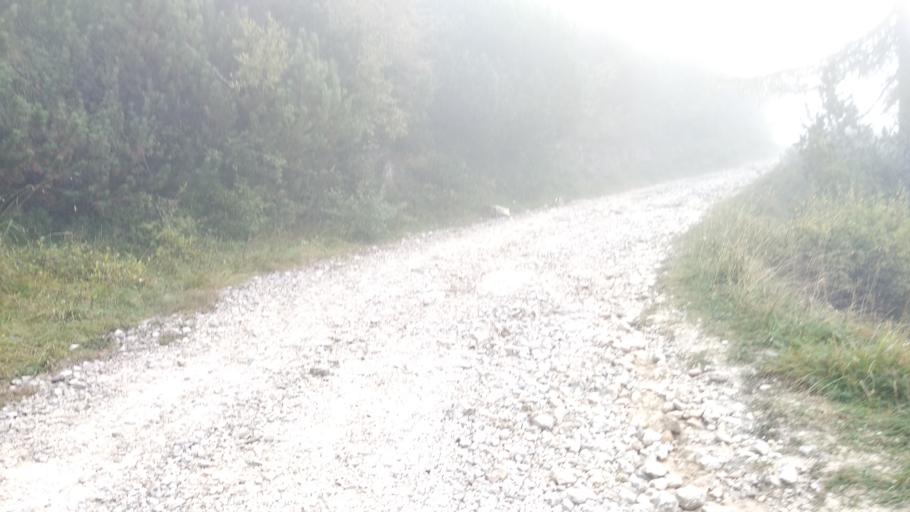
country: IT
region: Veneto
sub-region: Provincia di Vicenza
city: Roana
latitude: 45.9583
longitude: 11.4501
